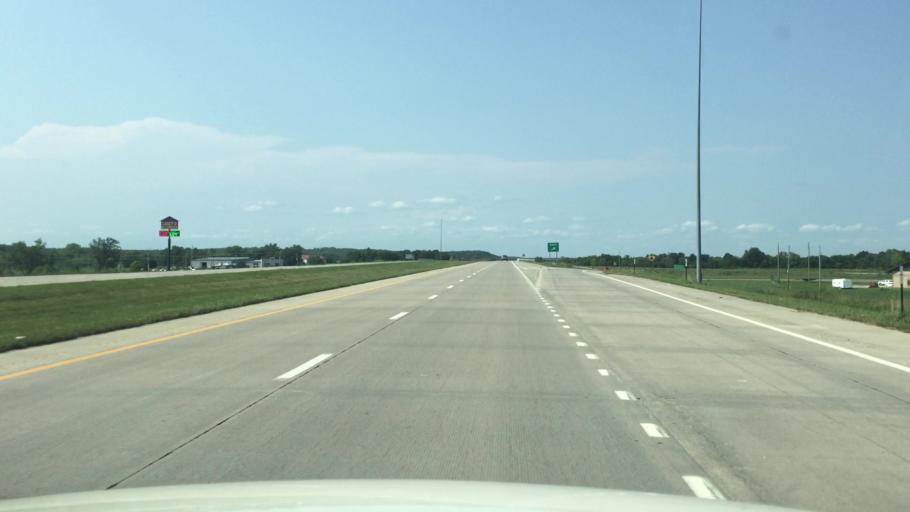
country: US
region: Kansas
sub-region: Linn County
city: Pleasanton
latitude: 38.1789
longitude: -94.6982
